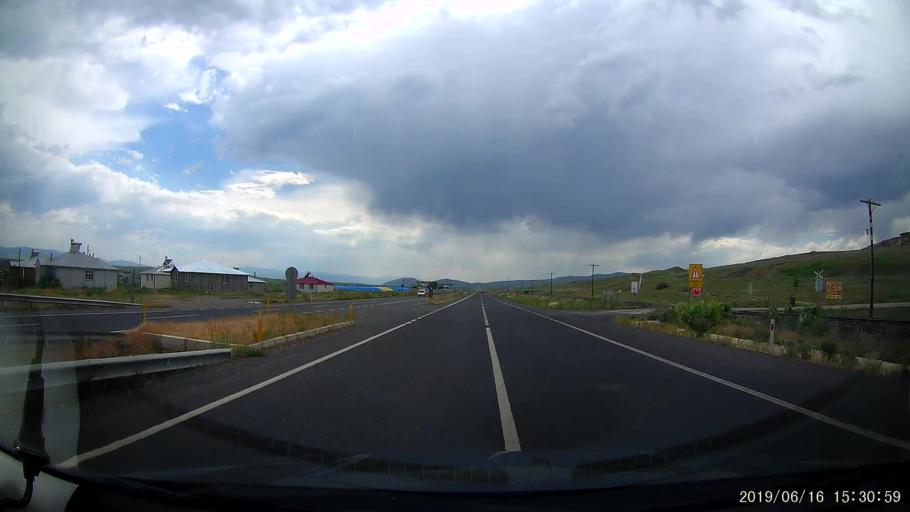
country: TR
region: Erzurum
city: Horasan
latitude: 40.0342
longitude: 42.0905
